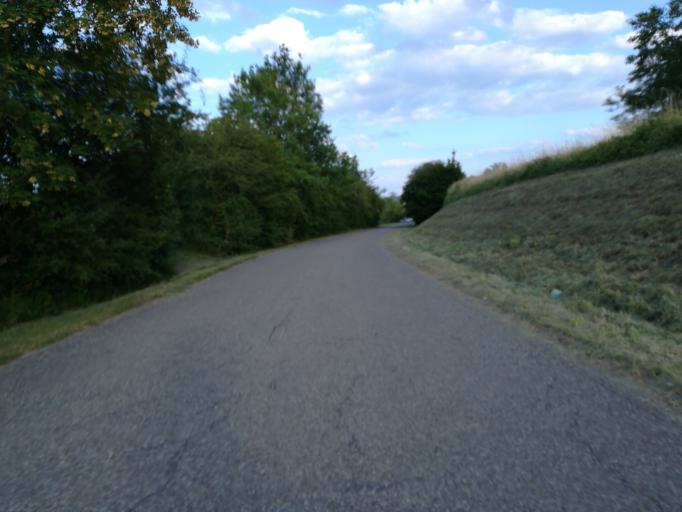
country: DE
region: Baden-Wuerttemberg
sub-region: Freiburg Region
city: Singen
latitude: 47.7577
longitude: 8.8296
